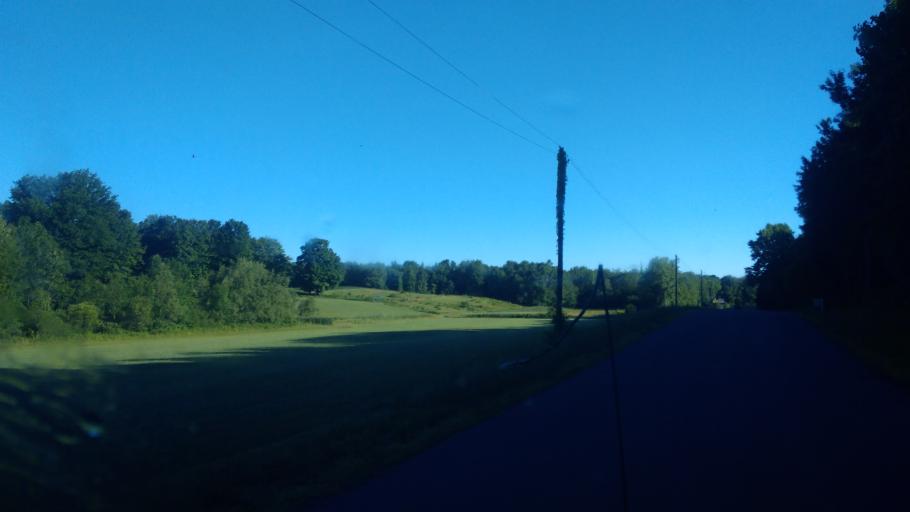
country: US
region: New York
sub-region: Wayne County
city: Lyons
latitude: 43.1421
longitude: -77.0426
